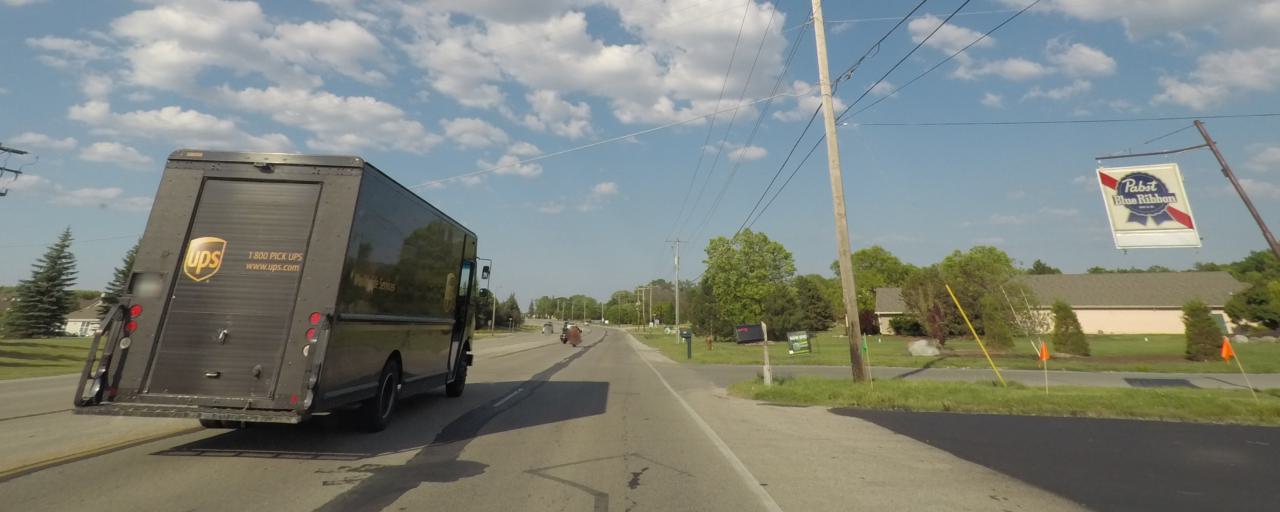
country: US
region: Wisconsin
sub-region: Milwaukee County
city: Hales Corners
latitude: 42.9310
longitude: -88.0742
